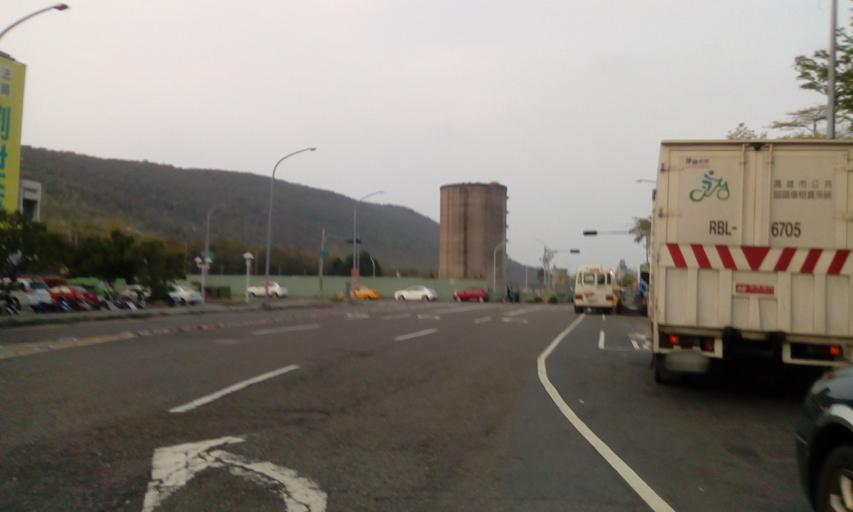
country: TW
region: Kaohsiung
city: Kaohsiung
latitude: 22.6884
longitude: 120.3073
